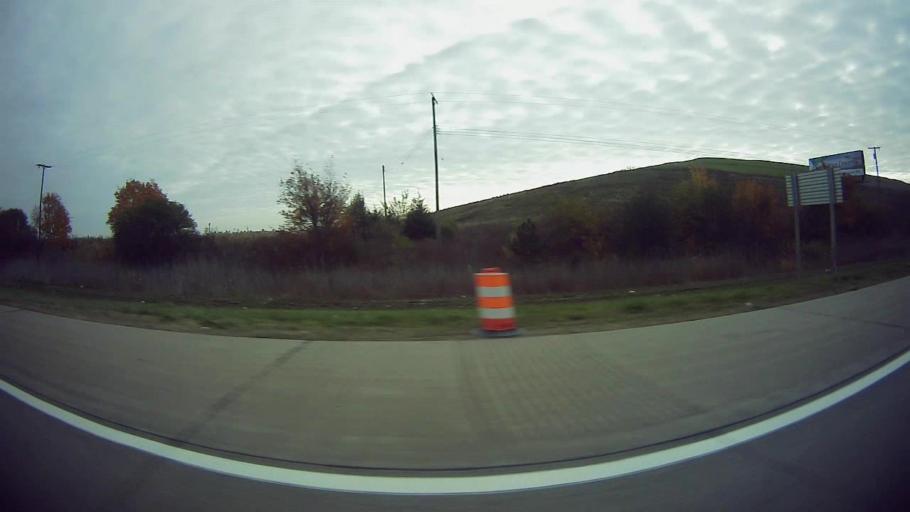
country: US
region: Michigan
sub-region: Wayne County
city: Woodhaven
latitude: 42.1911
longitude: -83.2419
